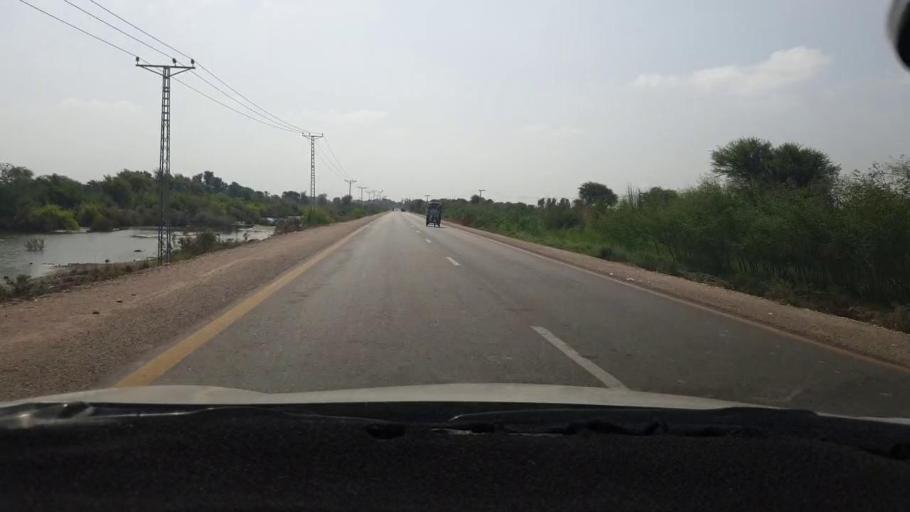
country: PK
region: Sindh
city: Mirpur Khas
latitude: 25.7296
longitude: 69.1074
